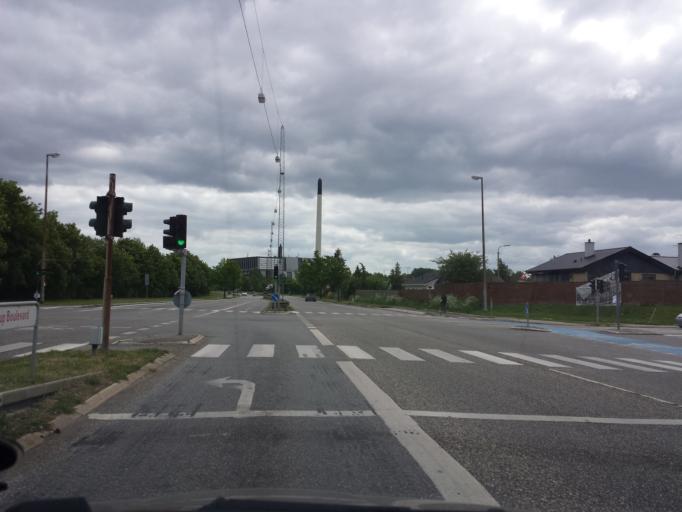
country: DK
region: Capital Region
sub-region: Herlev Kommune
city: Herlev
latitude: 55.7136
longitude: 12.4170
